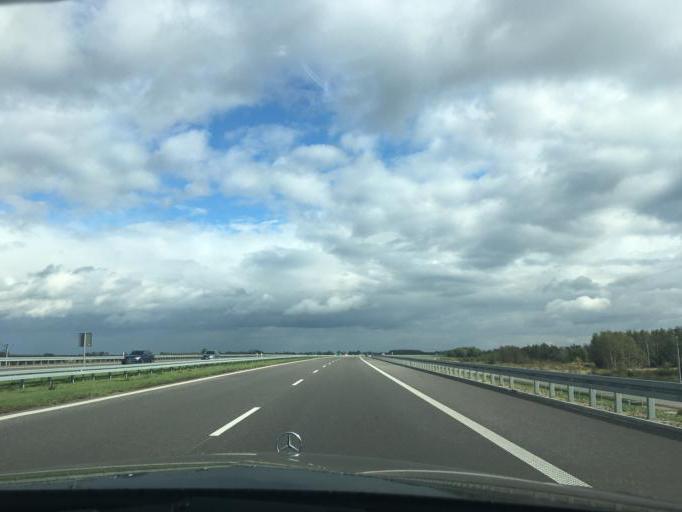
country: PL
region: Subcarpathian Voivodeship
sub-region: Powiat rzeszowski
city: Wolka Podlesna
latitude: 50.0953
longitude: 22.1101
